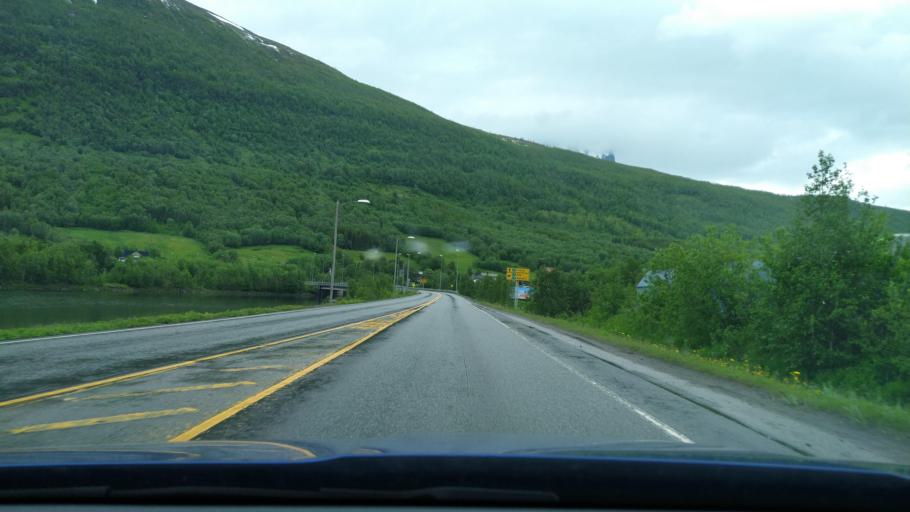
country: NO
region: Troms
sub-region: Balsfjord
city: Storsteinnes
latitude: 69.2161
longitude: 19.5533
